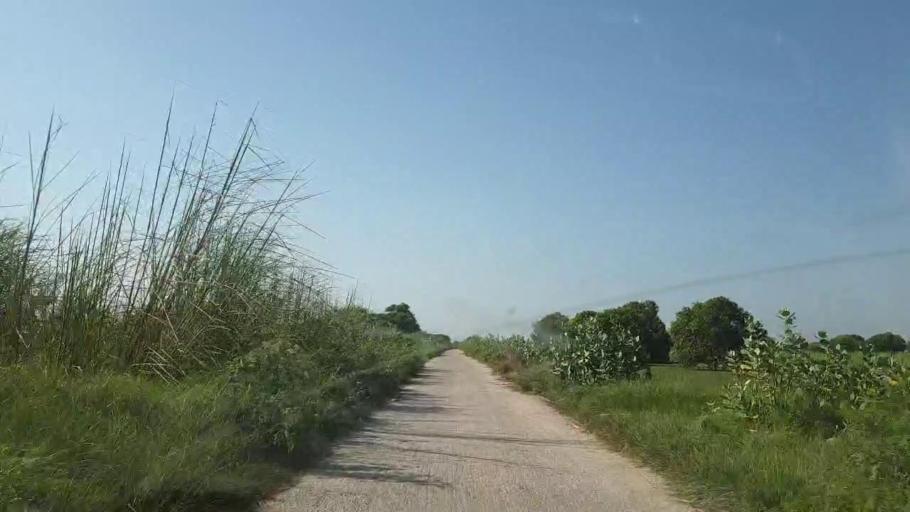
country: PK
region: Sindh
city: Tando Jam
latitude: 25.3335
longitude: 68.5872
